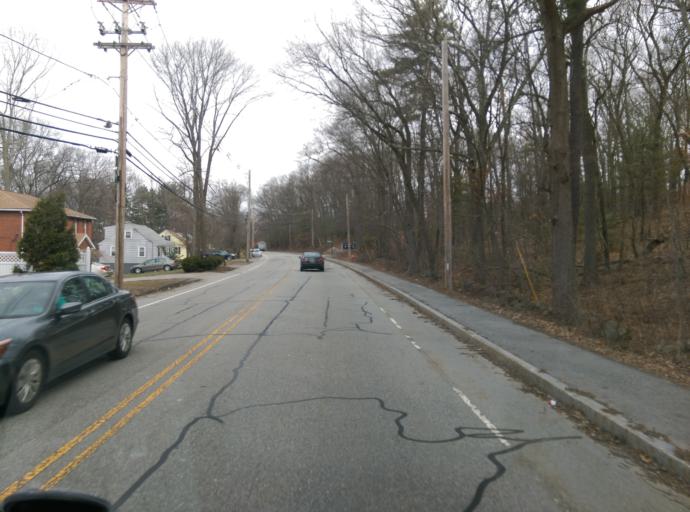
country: US
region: Massachusetts
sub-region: Essex County
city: North Andover
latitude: 42.6816
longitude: -71.1332
